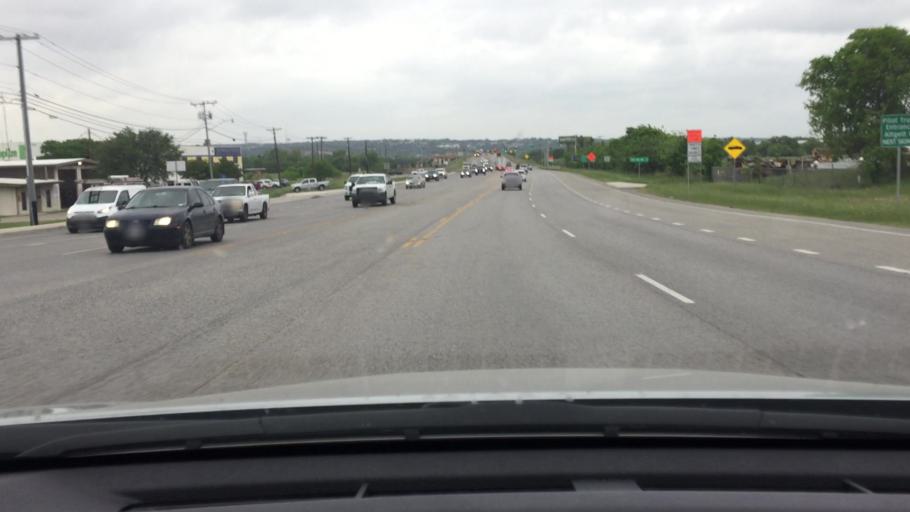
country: US
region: Texas
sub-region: Comal County
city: New Braunfels
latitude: 29.6760
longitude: -98.1551
